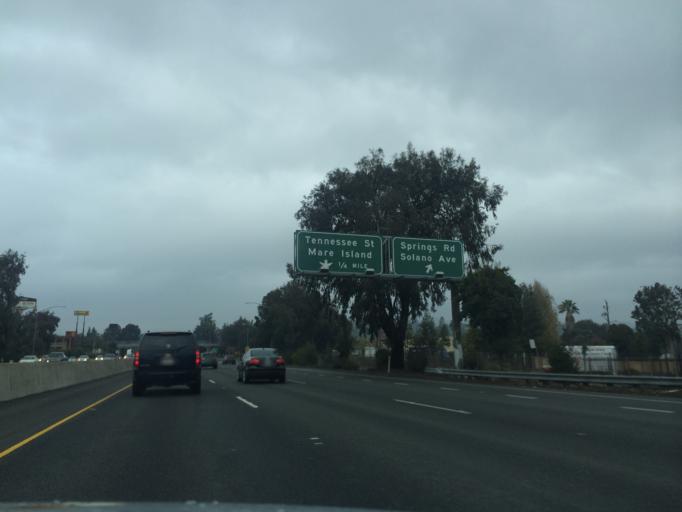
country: US
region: California
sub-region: Solano County
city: Vallejo
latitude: 38.1025
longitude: -122.2297
